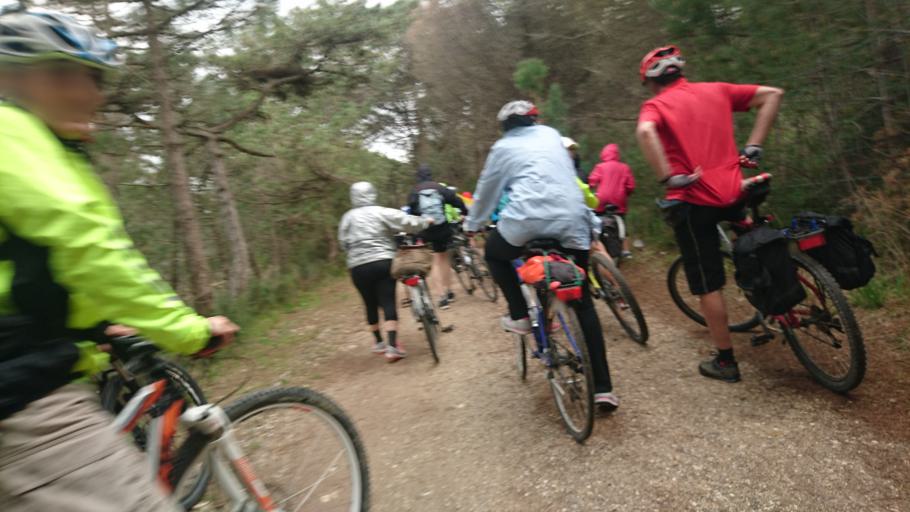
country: IT
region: Friuli Venezia Giulia
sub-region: Provincia di Udine
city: Lignano Sabbiadoro
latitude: 45.6444
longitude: 13.0947
